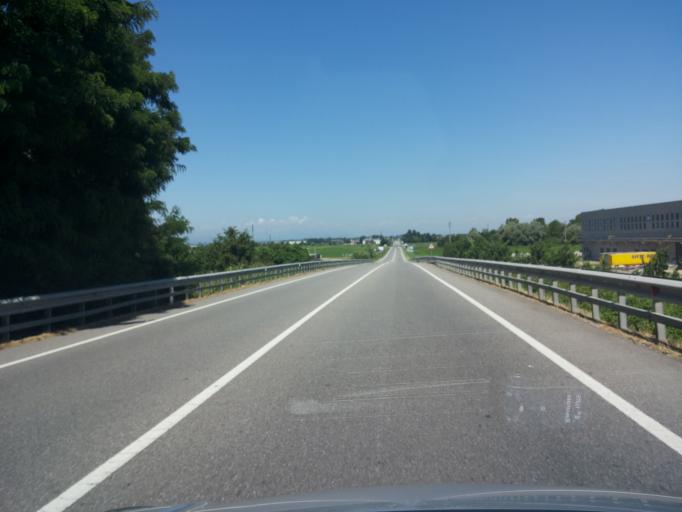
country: IT
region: Piedmont
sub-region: Provincia di Vercelli
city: Caresanablot
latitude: 45.3294
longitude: 8.3899
